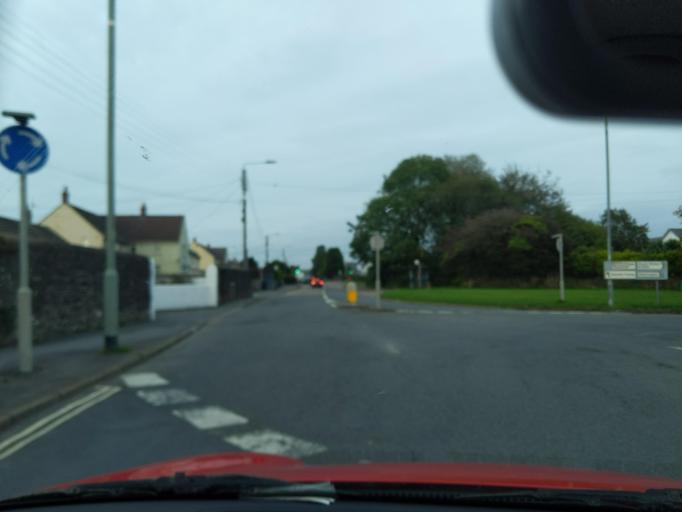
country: GB
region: England
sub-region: Devon
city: Great Torrington
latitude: 50.9547
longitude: -4.1361
